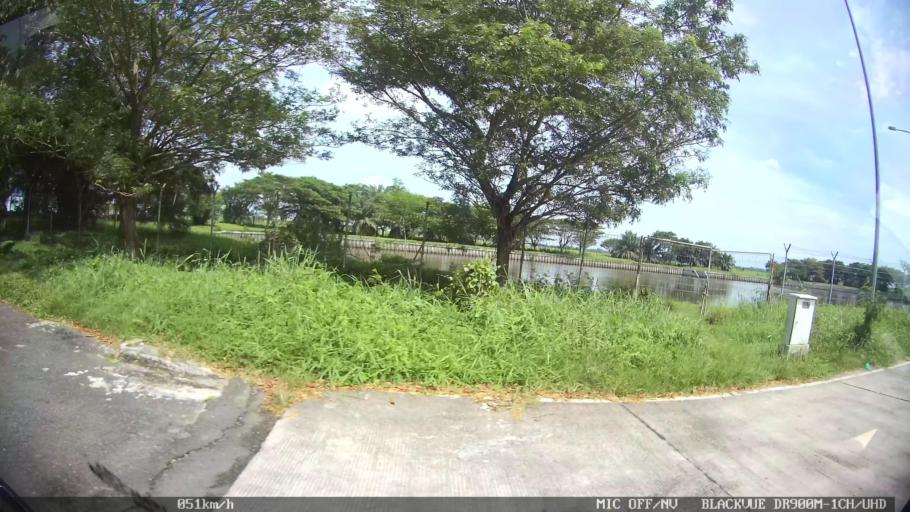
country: ID
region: North Sumatra
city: Percut
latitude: 3.6315
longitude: 98.8720
